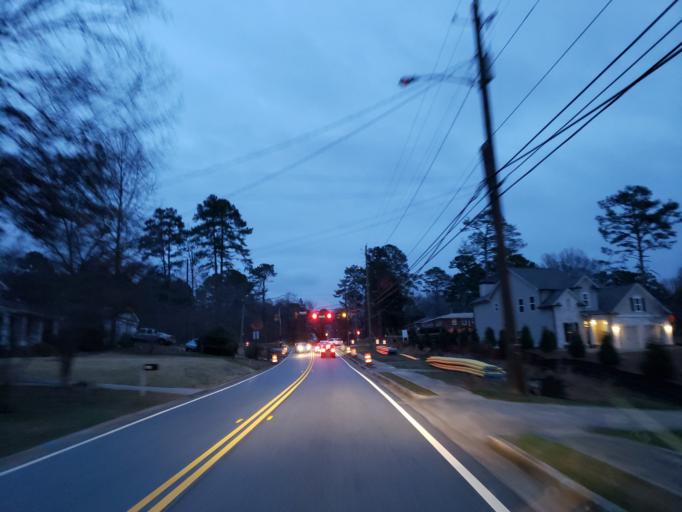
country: US
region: Georgia
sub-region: Cobb County
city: Mableton
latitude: 33.8448
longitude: -84.5797
